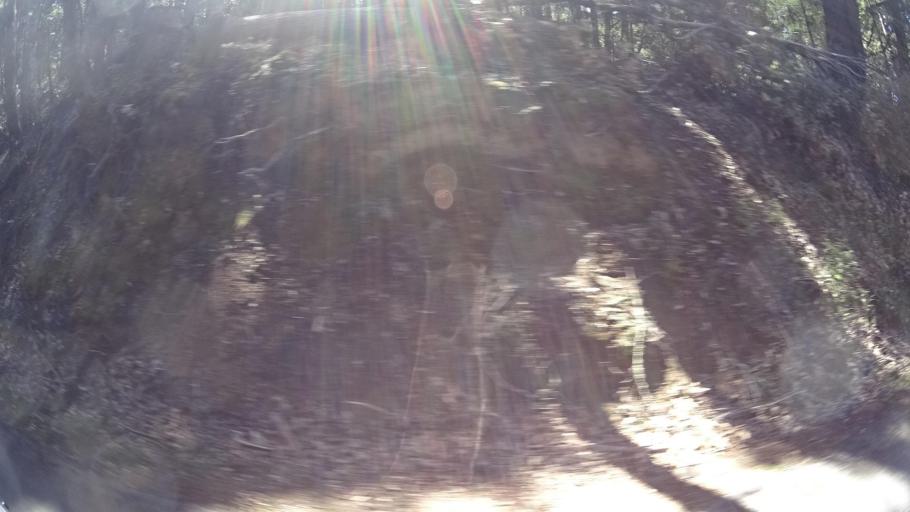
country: US
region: California
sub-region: Humboldt County
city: Rio Dell
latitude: 40.3039
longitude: -124.0622
